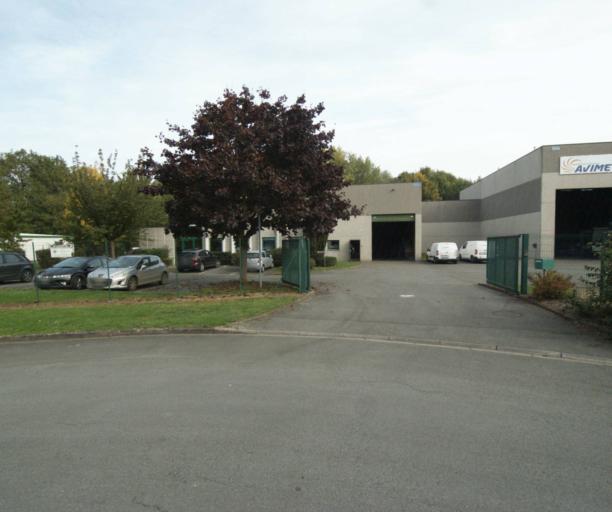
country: FR
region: Nord-Pas-de-Calais
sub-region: Departement du Nord
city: Don
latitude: 50.5545
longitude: 2.9275
